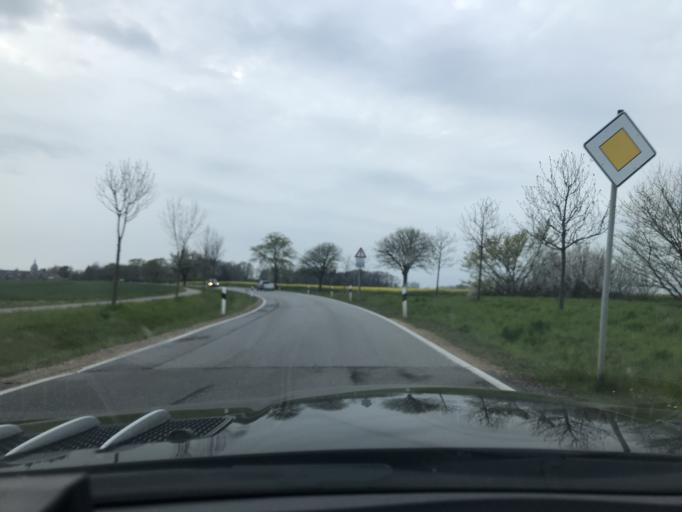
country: DE
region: Schleswig-Holstein
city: Burg auf Fehmarn
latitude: 54.4329
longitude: 11.2146
